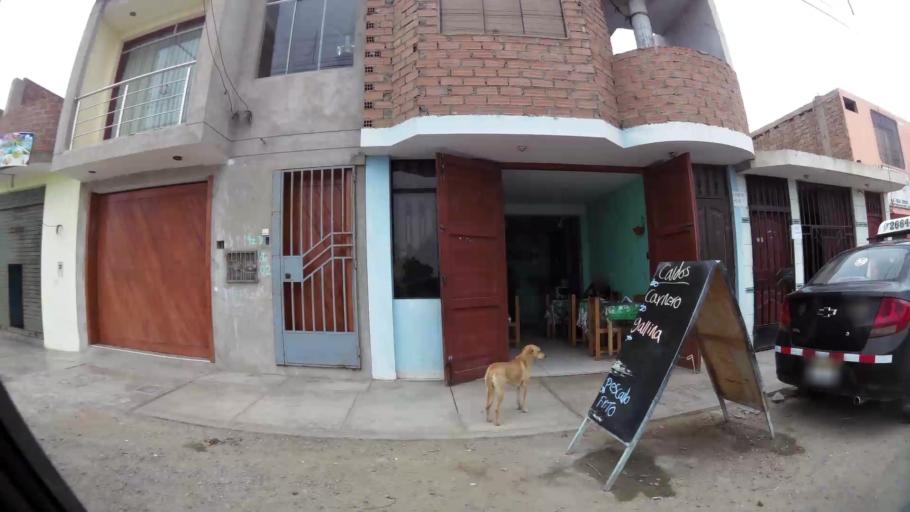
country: PE
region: La Libertad
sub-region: Provincia de Trujillo
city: Huanchaco
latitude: -8.0902
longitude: -79.0870
